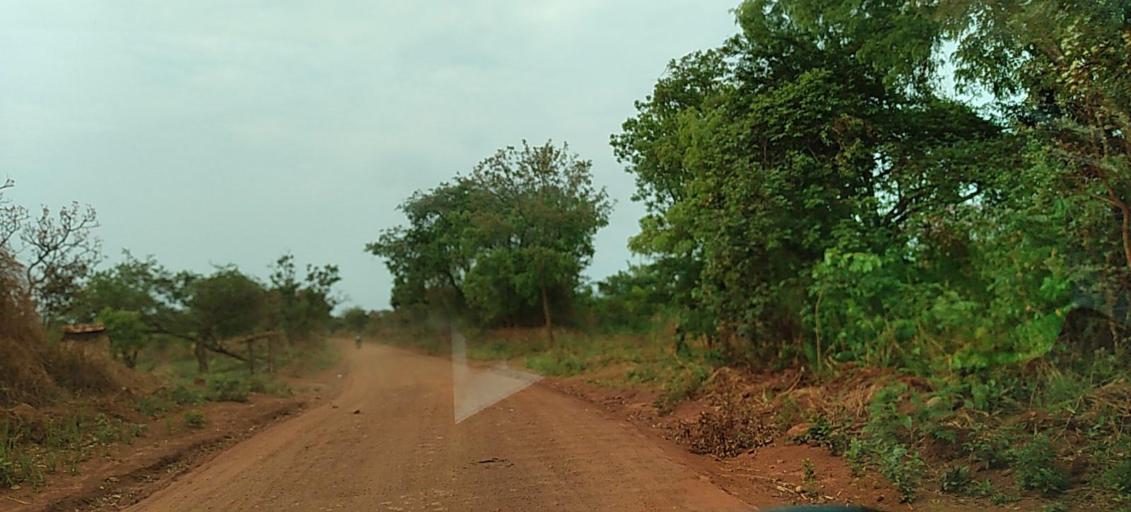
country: ZM
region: North-Western
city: Solwezi
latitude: -12.2264
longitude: 26.5104
